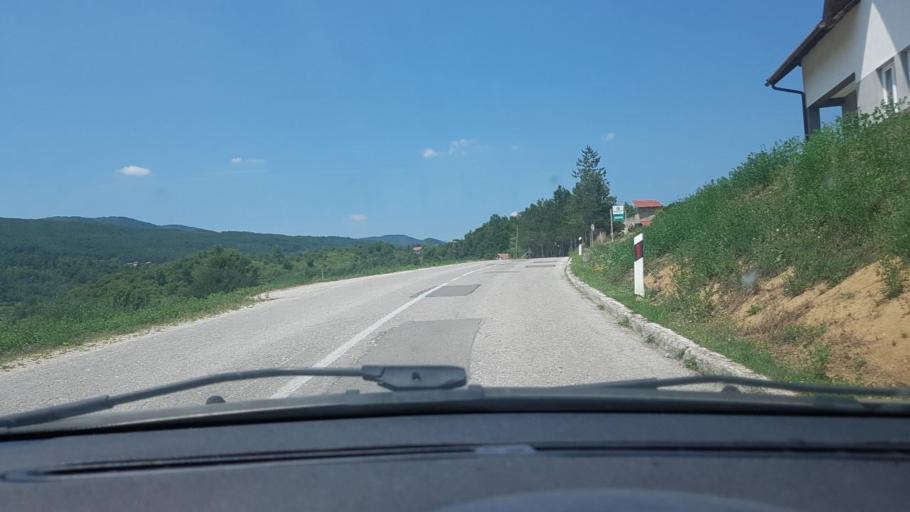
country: BA
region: Federation of Bosnia and Herzegovina
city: Orasac
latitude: 44.5936
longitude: 16.0796
